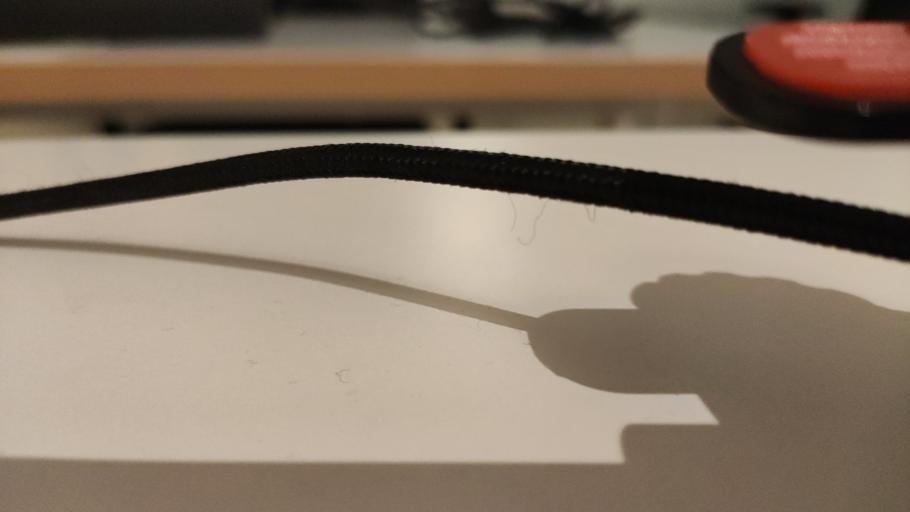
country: RU
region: Moskovskaya
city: Budenovetc
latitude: 56.3812
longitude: 37.6033
